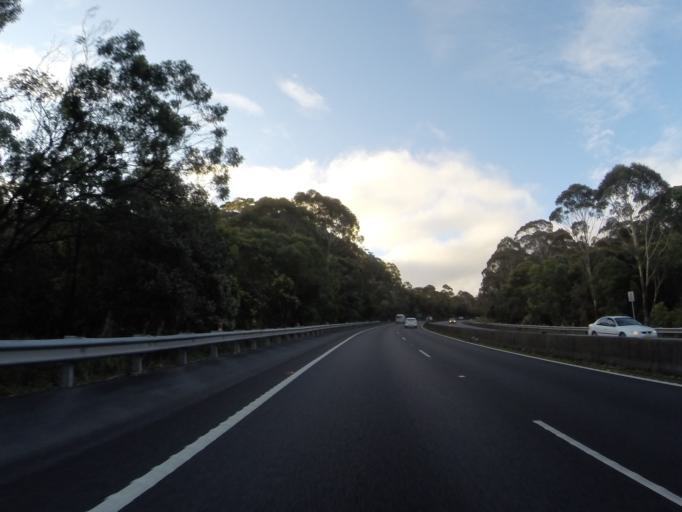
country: AU
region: New South Wales
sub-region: Wollongong
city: Bulli
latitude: -34.3291
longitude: 150.8765
